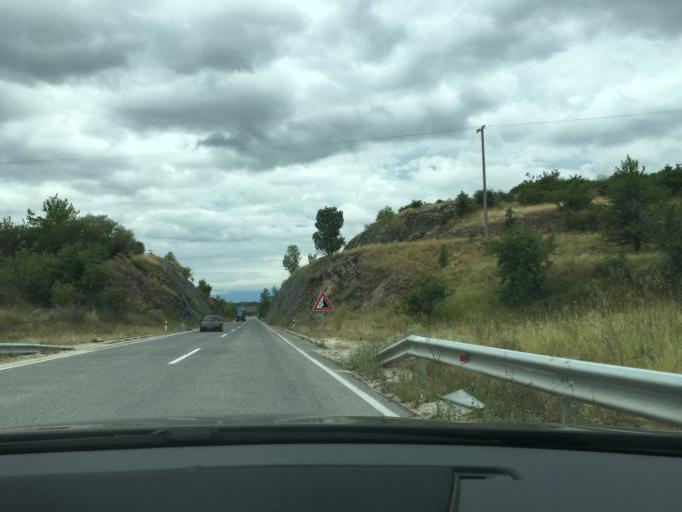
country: MK
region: Opstina Rankovce
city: Rankovce
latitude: 42.1470
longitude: 22.0123
